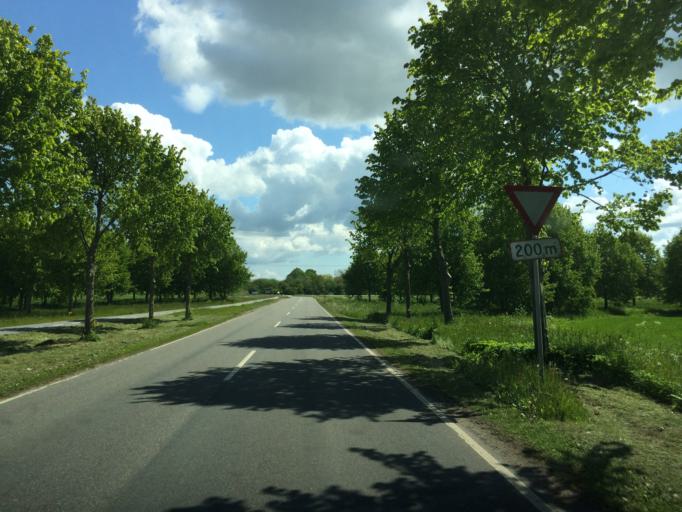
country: DK
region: Zealand
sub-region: Roskilde Kommune
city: Svogerslev
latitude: 55.6231
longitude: 12.0452
